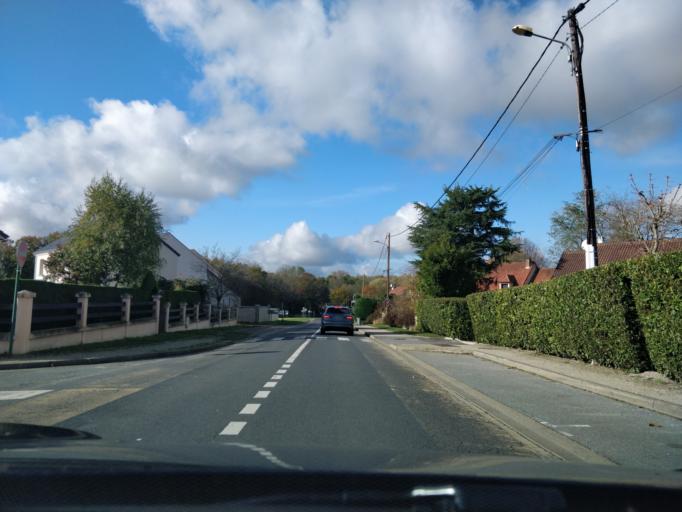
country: FR
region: Ile-de-France
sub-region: Departement de l'Essonne
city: Fontenay-les-Briis
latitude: 48.6135
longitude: 2.1641
